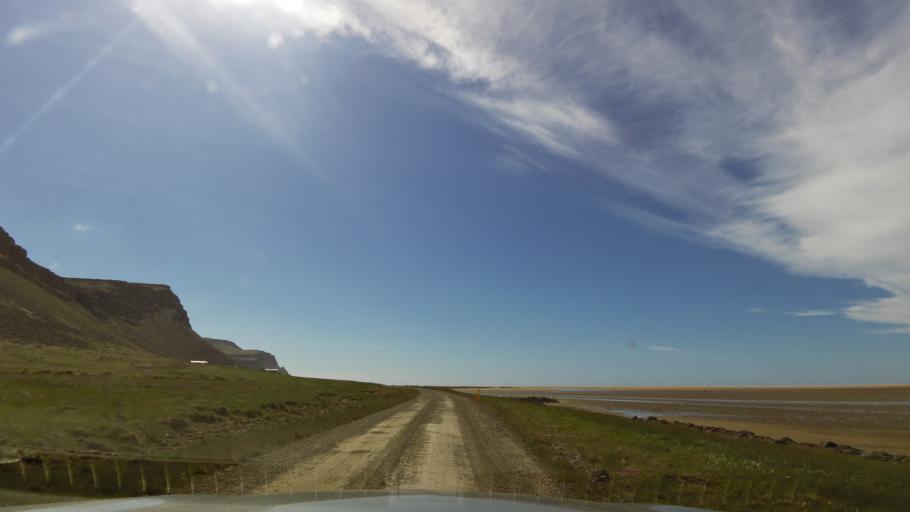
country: IS
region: West
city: Olafsvik
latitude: 65.4524
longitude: -23.9476
